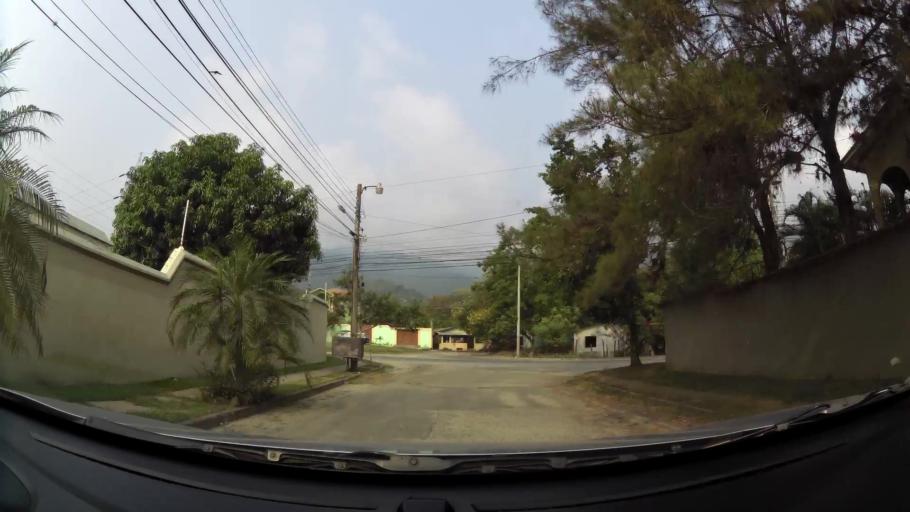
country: HN
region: Cortes
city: Armenta
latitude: 15.4879
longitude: -88.0434
